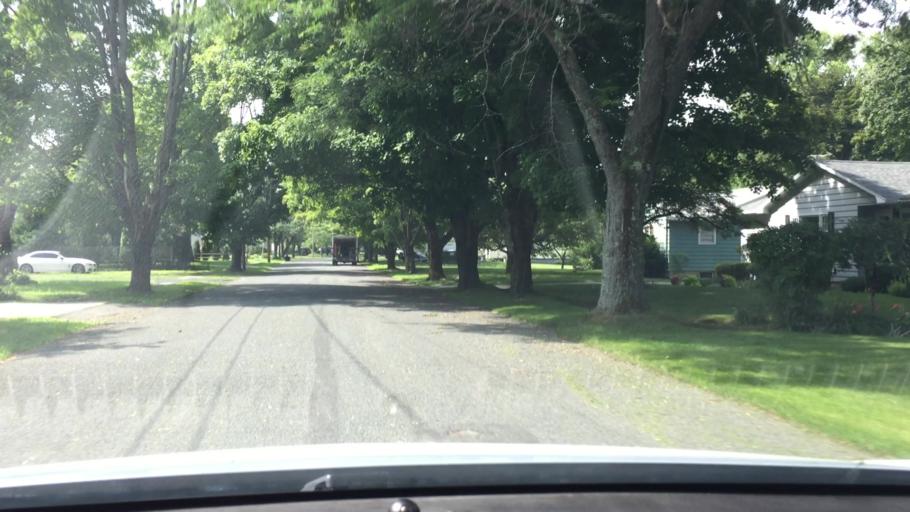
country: US
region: Massachusetts
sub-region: Berkshire County
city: Pittsfield
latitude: 42.4360
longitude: -73.2117
